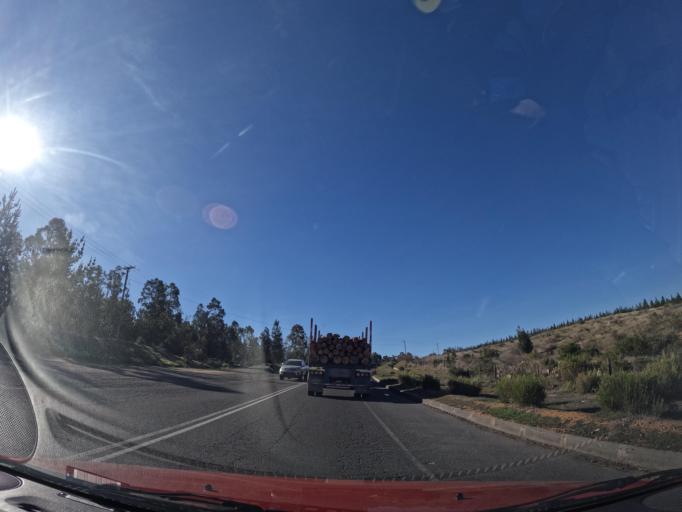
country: CL
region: Maule
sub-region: Provincia de Cauquenes
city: Cauquenes
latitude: -35.9326
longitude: -72.1937
